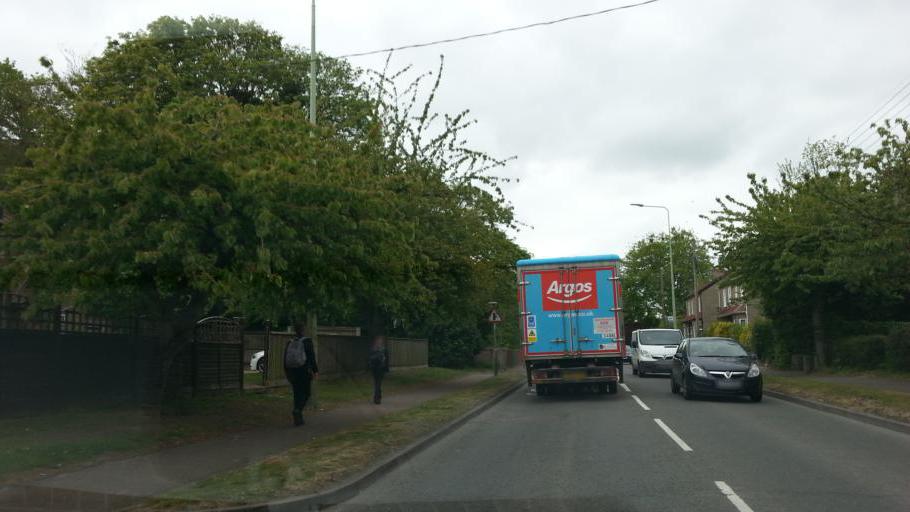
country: GB
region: England
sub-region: Suffolk
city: Lakenheath
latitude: 52.3444
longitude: 0.5163
